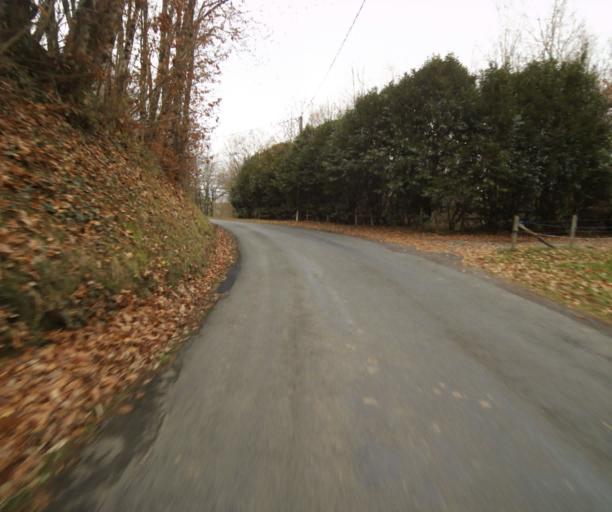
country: FR
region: Limousin
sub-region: Departement de la Correze
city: Chameyrat
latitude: 45.2492
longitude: 1.6841
